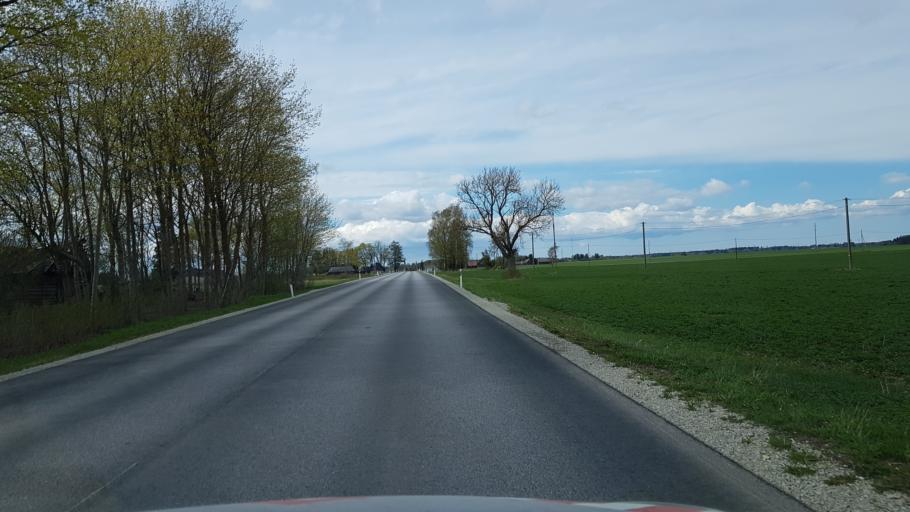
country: EE
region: Laeaene-Virumaa
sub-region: Vinni vald
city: Vinni
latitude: 59.2335
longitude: 26.5049
